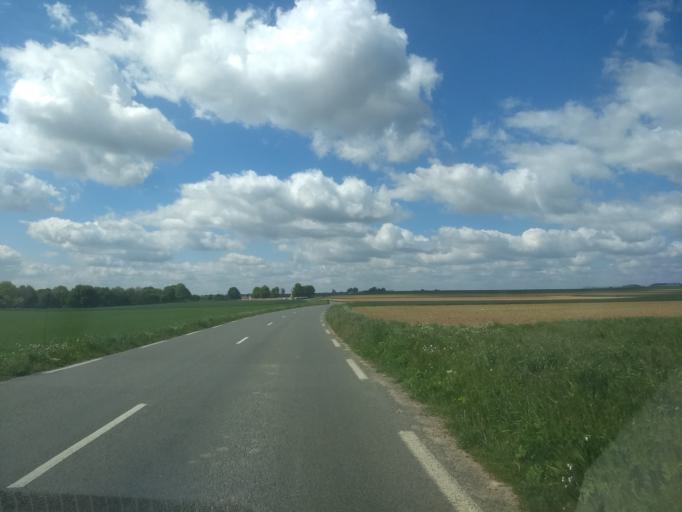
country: FR
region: Nord-Pas-de-Calais
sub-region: Departement du Pas-de-Calais
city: Saint-Laurent-Blangy
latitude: 50.3232
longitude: 2.8211
